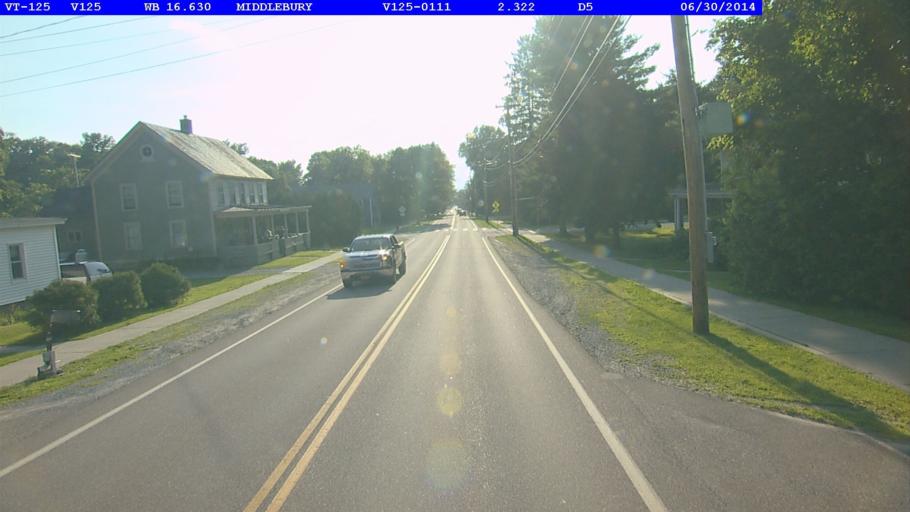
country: US
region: Vermont
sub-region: Addison County
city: Middlebury (village)
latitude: 43.9719
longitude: -73.0954
